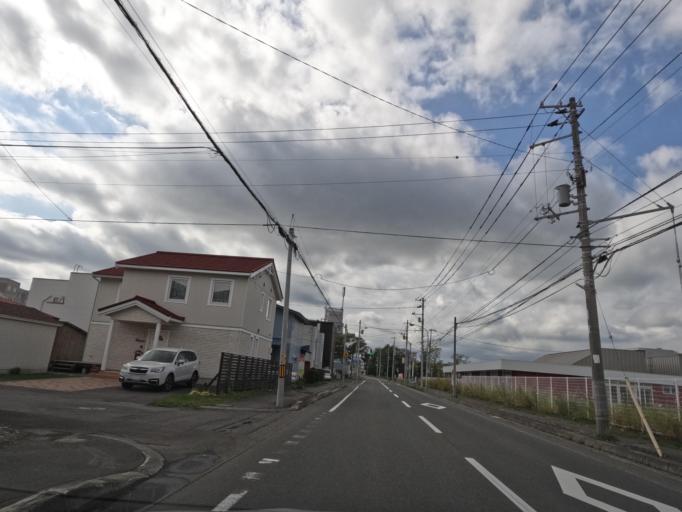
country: JP
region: Hokkaido
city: Chitose
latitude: 42.8212
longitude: 141.6364
